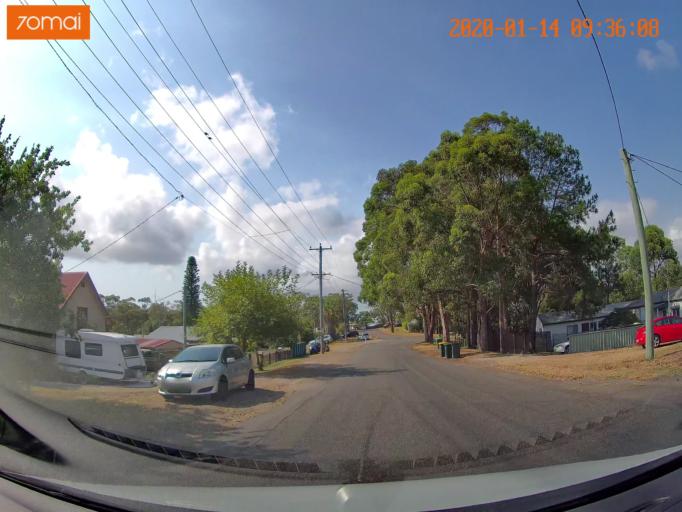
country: AU
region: New South Wales
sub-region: Lake Macquarie Shire
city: Arcadia vale
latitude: -33.1096
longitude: 151.5560
